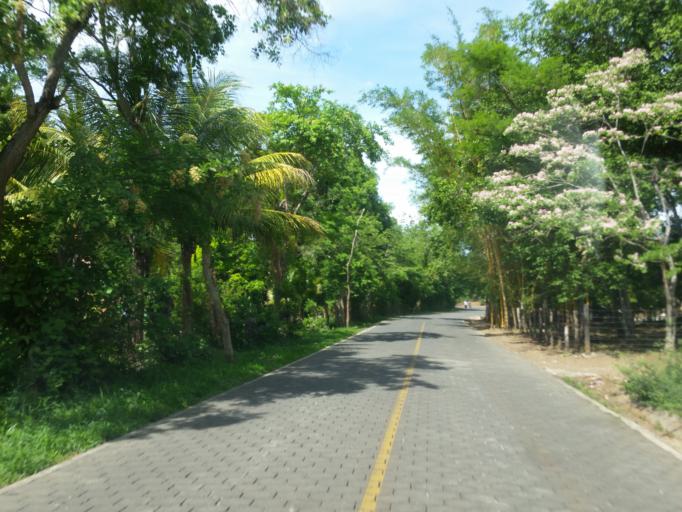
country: NI
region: Masaya
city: Masaya
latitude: 11.9625
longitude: -86.0406
